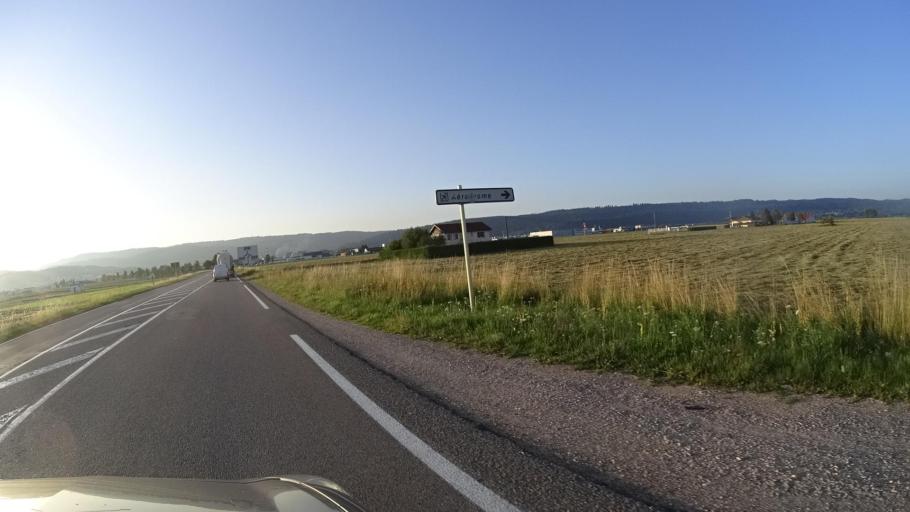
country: FR
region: Franche-Comte
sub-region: Departement du Doubs
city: Doubs
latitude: 46.9117
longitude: 6.3269
